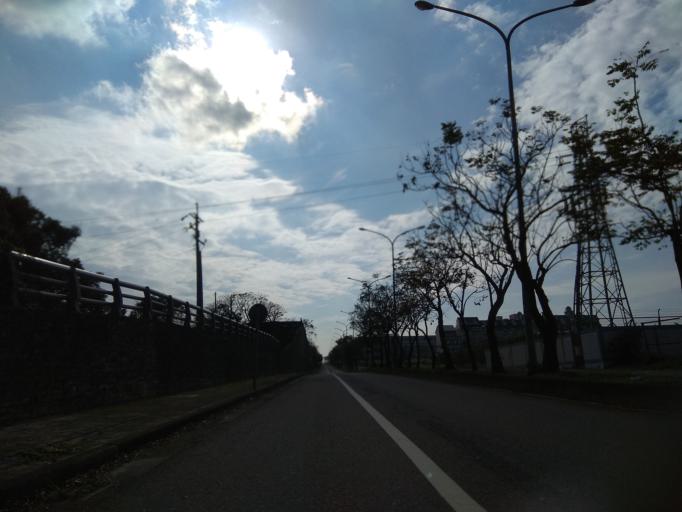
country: TW
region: Taiwan
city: Taoyuan City
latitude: 25.0531
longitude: 121.1794
